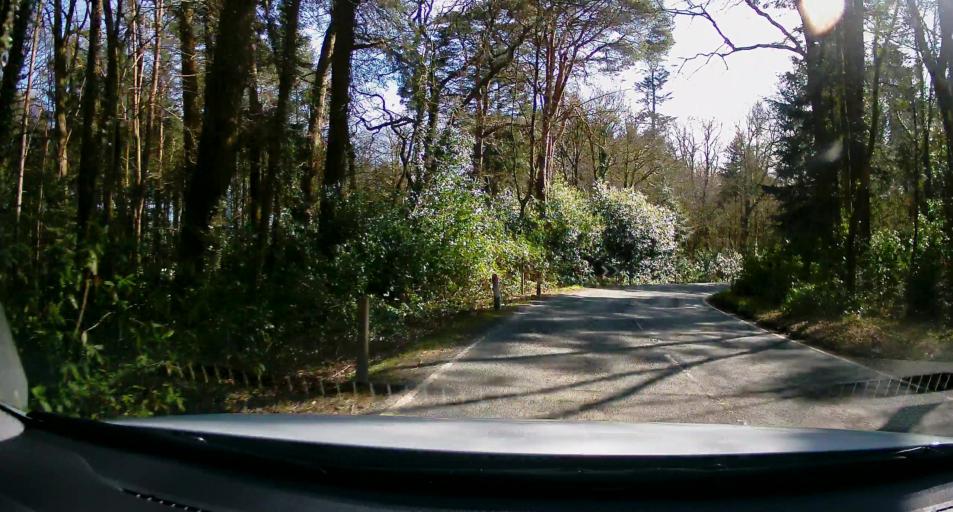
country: GB
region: Wales
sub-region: County of Ceredigion
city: Lledrod
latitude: 52.3439
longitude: -3.9584
